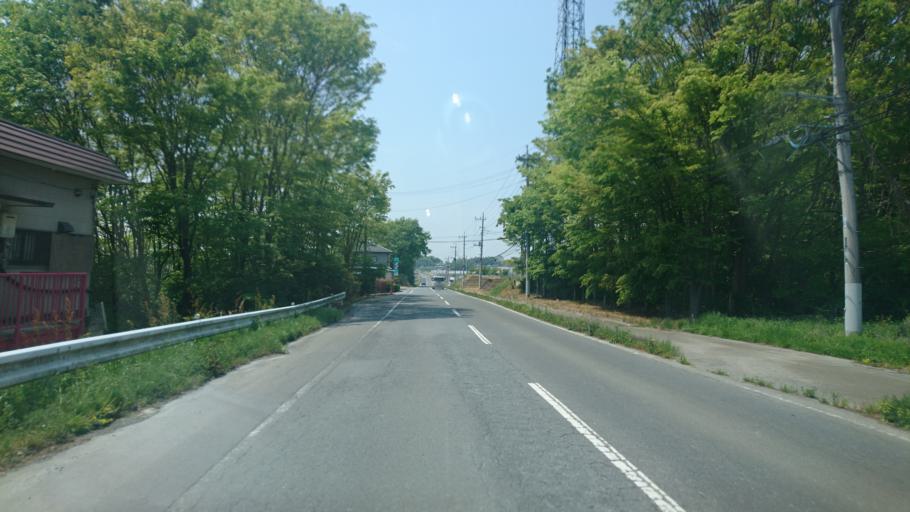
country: JP
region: Ibaraki
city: Shimodate
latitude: 36.2553
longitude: 139.9683
